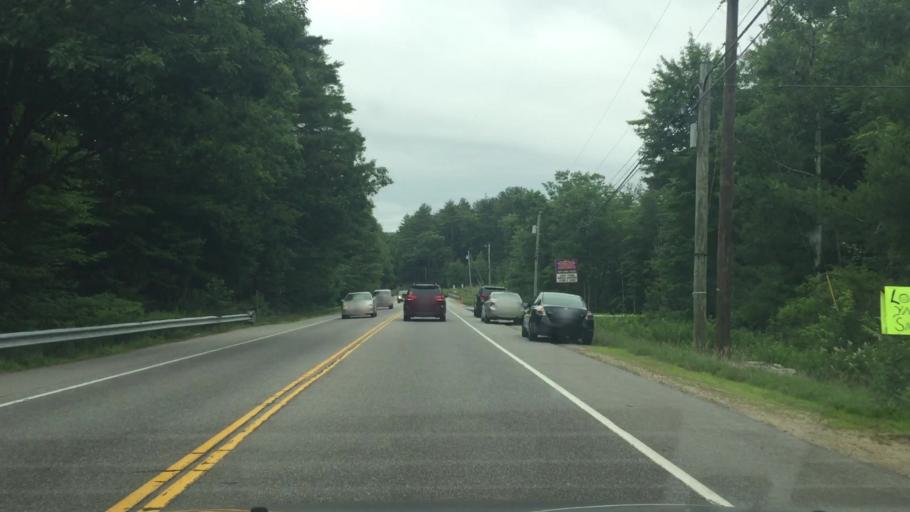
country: US
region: New Hampshire
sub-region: Grafton County
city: Ashland
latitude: 43.6243
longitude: -71.6163
